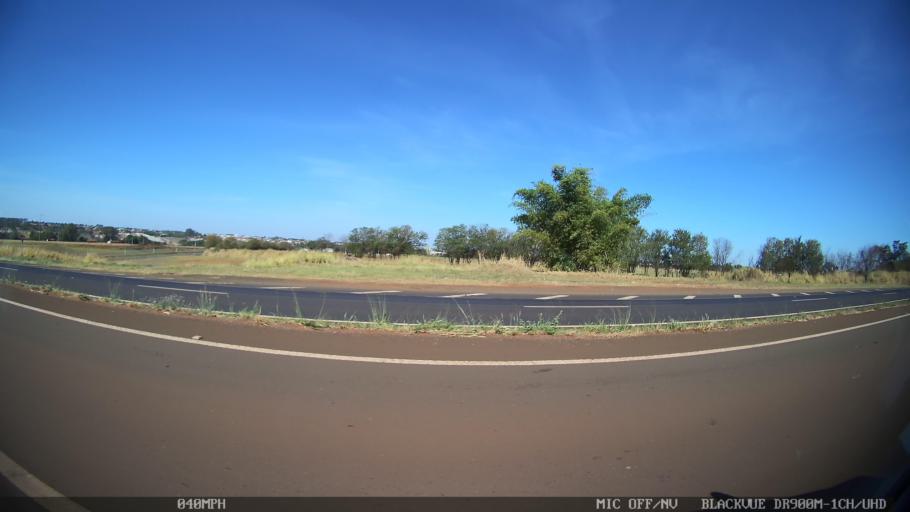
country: BR
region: Sao Paulo
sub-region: Barretos
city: Barretos
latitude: -20.5283
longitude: -48.5922
